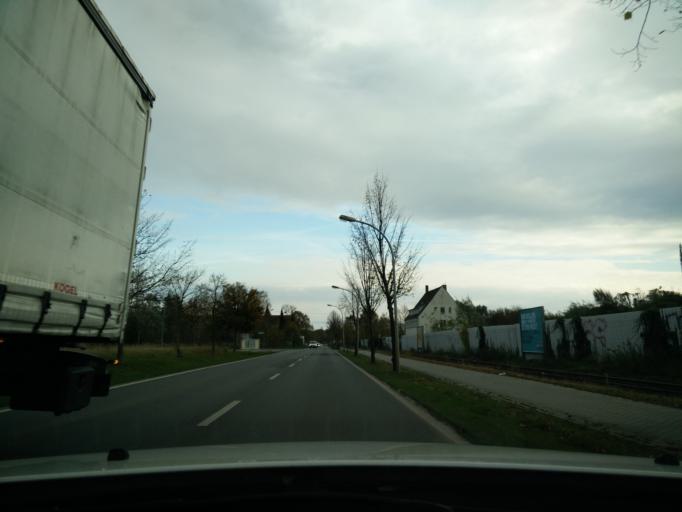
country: DE
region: Brandenburg
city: Velten
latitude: 52.6809
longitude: 13.1947
